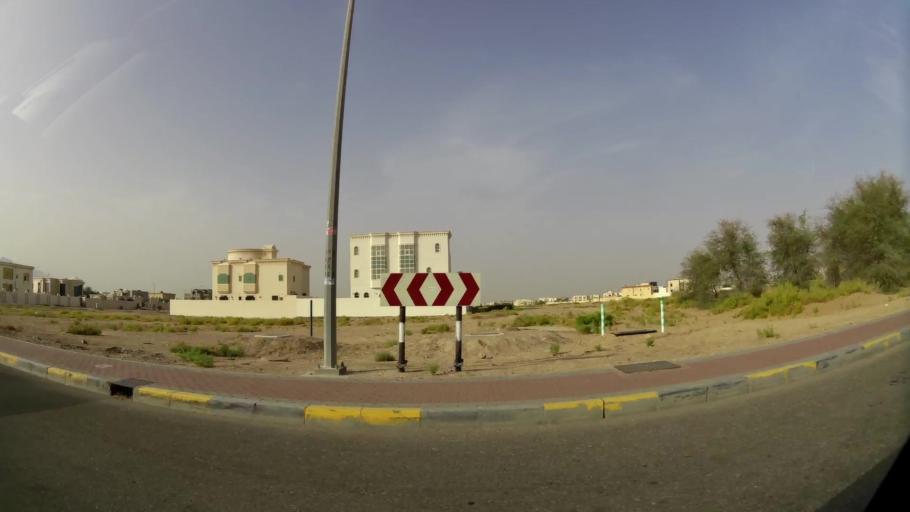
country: AE
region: Abu Dhabi
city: Al Ain
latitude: 24.1268
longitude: 55.7003
